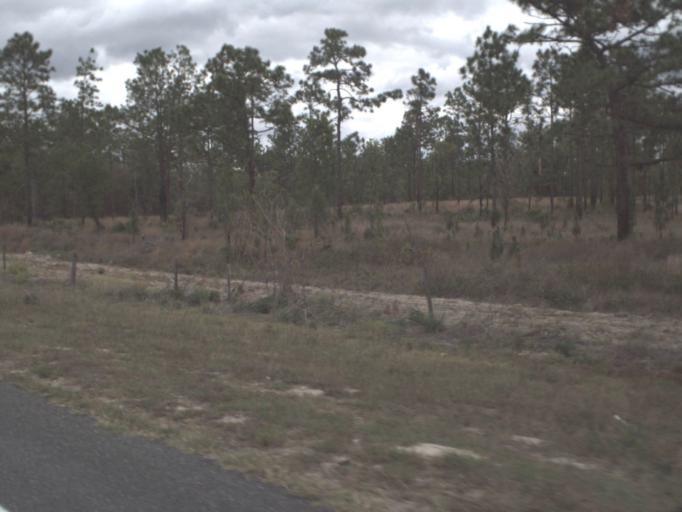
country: US
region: Florida
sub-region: Marion County
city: Ocala
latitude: 29.2487
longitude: -82.0621
